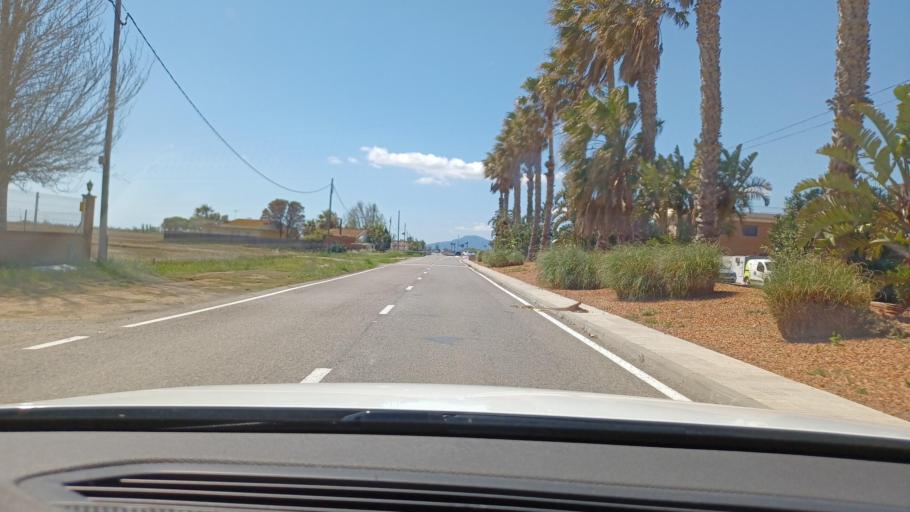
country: ES
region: Catalonia
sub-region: Provincia de Tarragona
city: L'Ampolla
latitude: 40.7992
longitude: 0.6975
